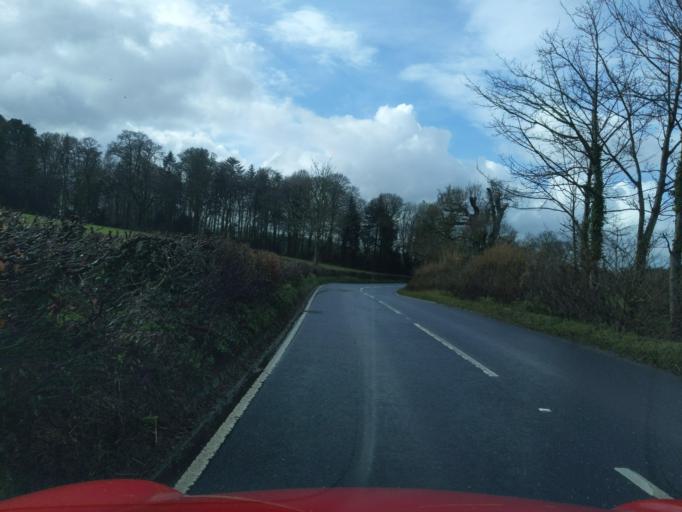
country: GB
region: England
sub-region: Devon
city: Great Torrington
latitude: 50.8760
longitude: -4.0837
